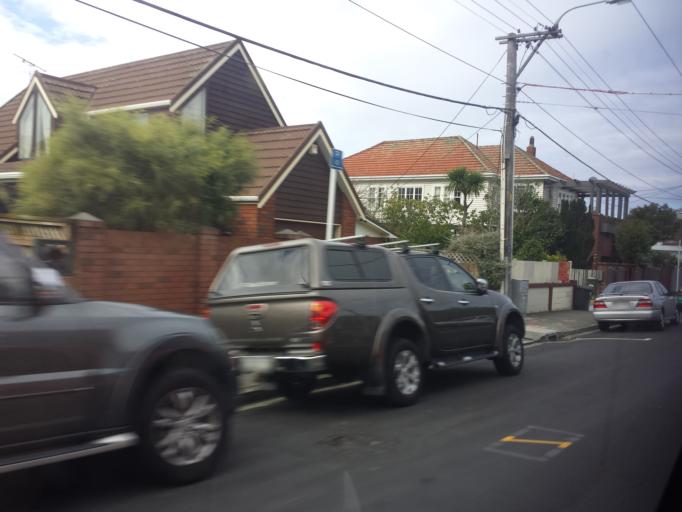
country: NZ
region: Wellington
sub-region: Wellington City
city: Wellington
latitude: -41.3050
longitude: 174.7938
